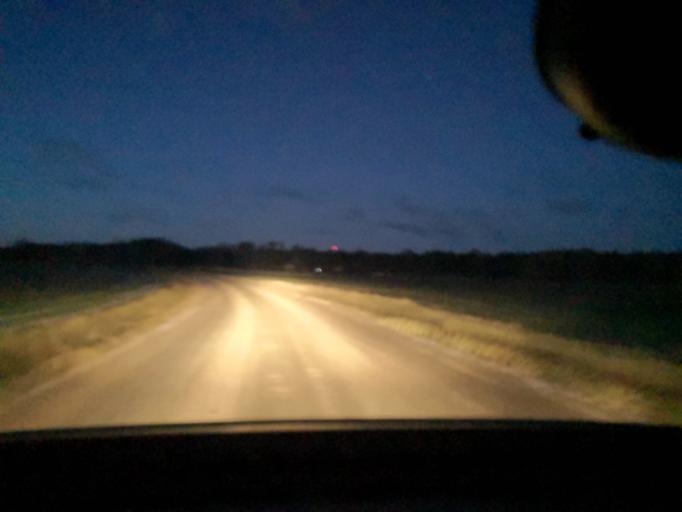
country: SE
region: Uppsala
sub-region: Heby Kommun
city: Heby
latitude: 59.9286
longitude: 16.7556
